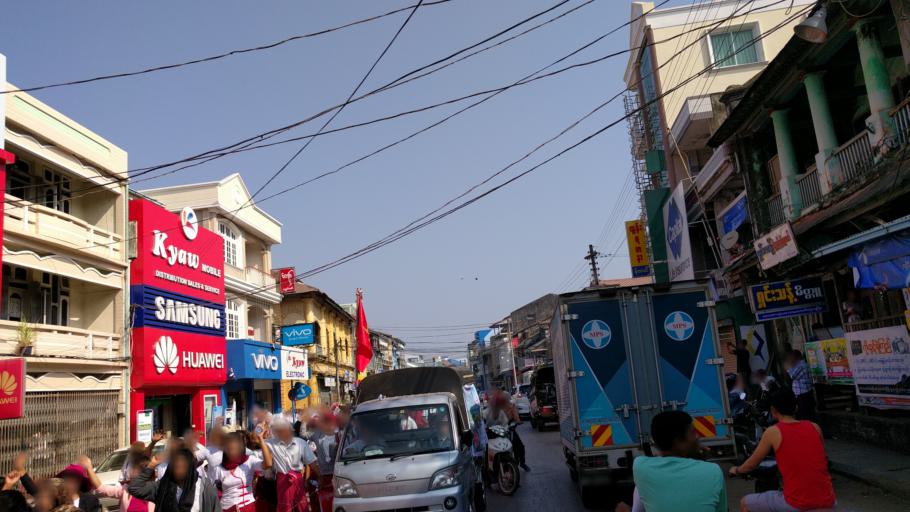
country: MM
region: Mon
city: Mawlamyine
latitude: 16.4879
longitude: 97.6191
